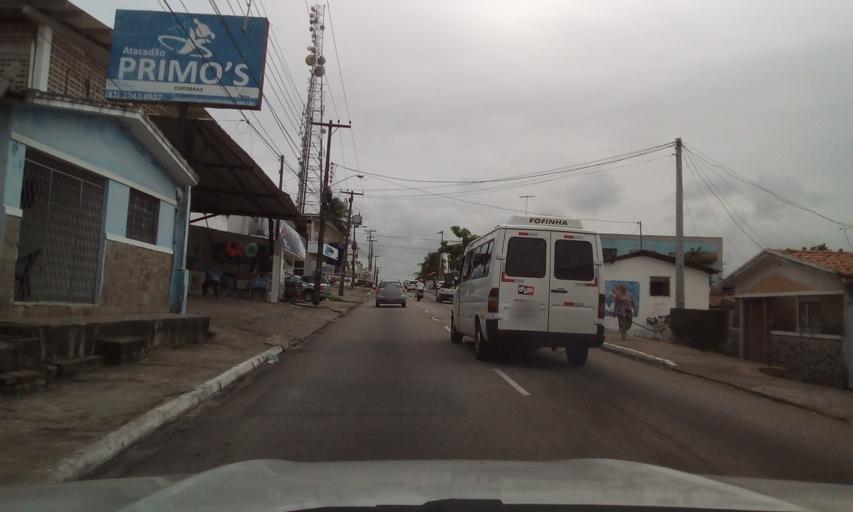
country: BR
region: Paraiba
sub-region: Joao Pessoa
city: Joao Pessoa
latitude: -7.1009
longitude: -34.8628
